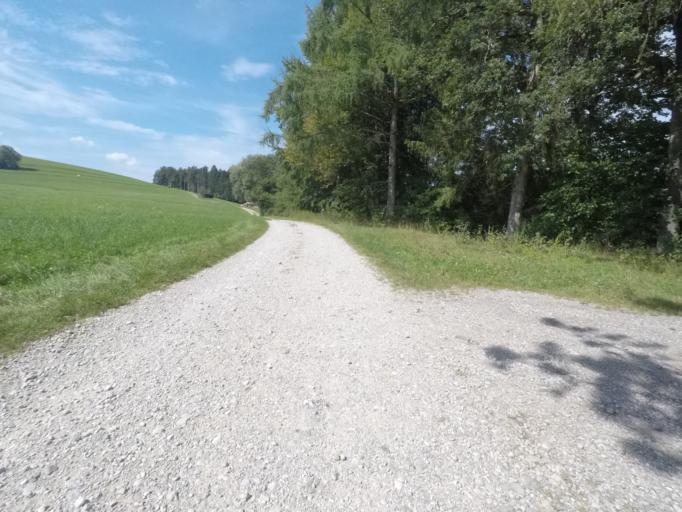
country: DE
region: Bavaria
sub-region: Upper Bavaria
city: Konigsdorf
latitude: 47.8262
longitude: 11.5105
